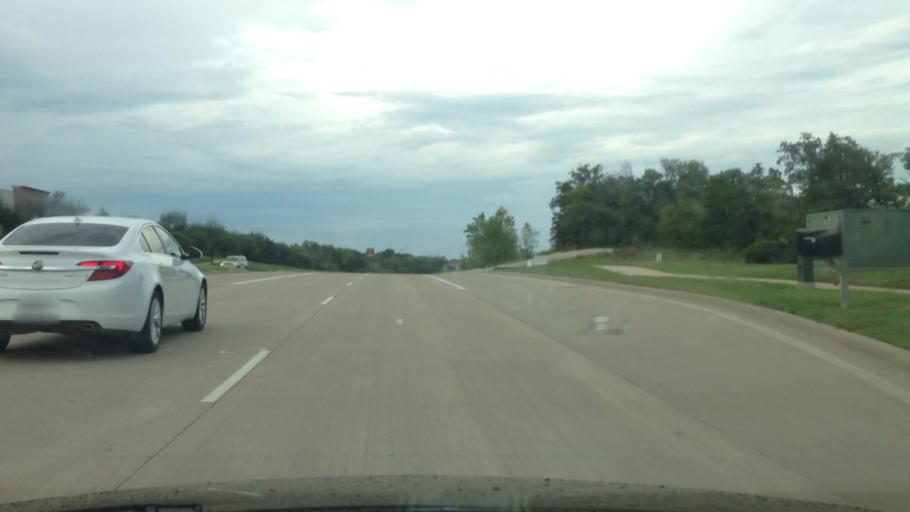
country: US
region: Texas
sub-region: Dallas County
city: Coppell
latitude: 32.9968
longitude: -97.0370
